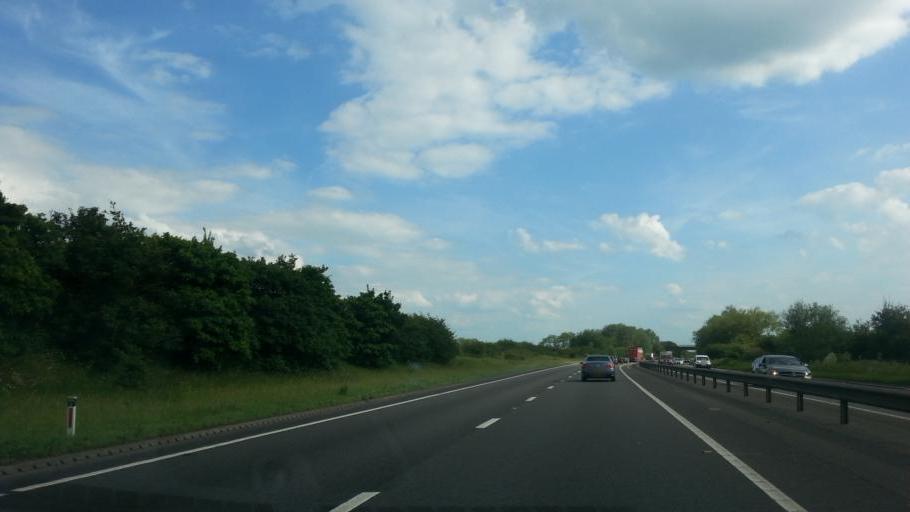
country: GB
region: England
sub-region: Nottinghamshire
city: South Collingham
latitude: 53.1486
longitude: -0.8045
